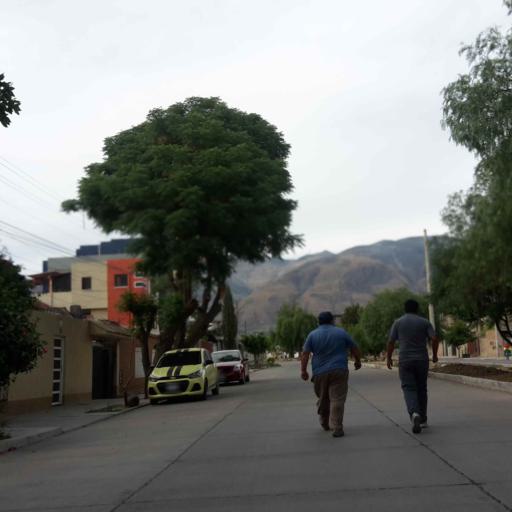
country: BO
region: Cochabamba
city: Cochabamba
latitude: -17.3690
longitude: -66.1897
